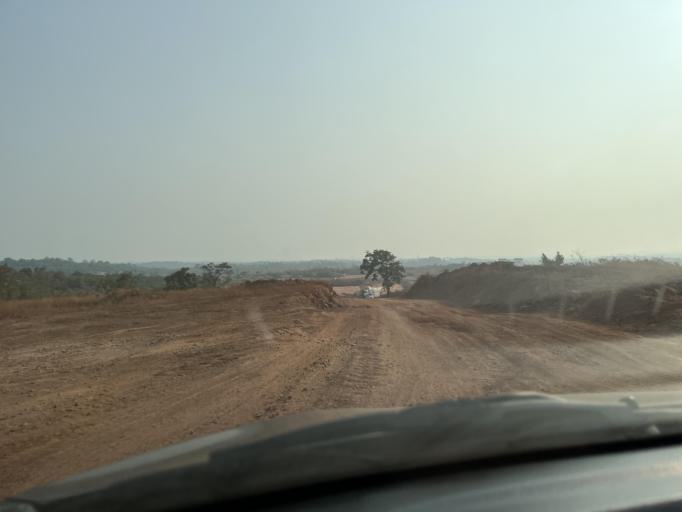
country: IN
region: Goa
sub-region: North Goa
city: Pernem
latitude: 15.6940
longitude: 73.8386
